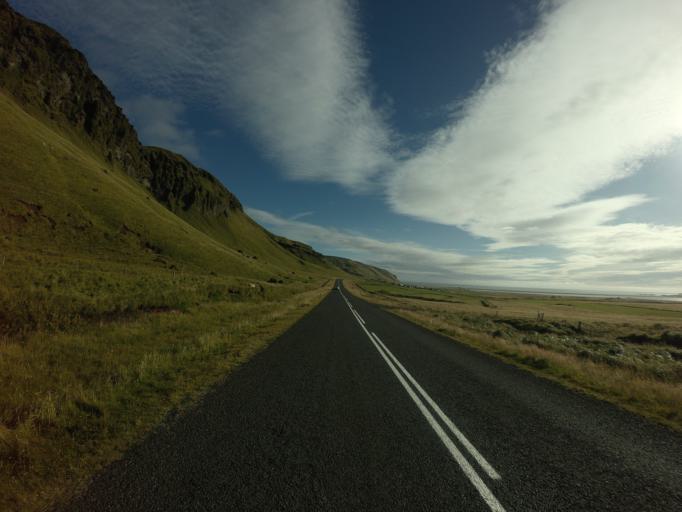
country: IS
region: South
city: Vestmannaeyjar
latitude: 63.4324
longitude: -19.0543
